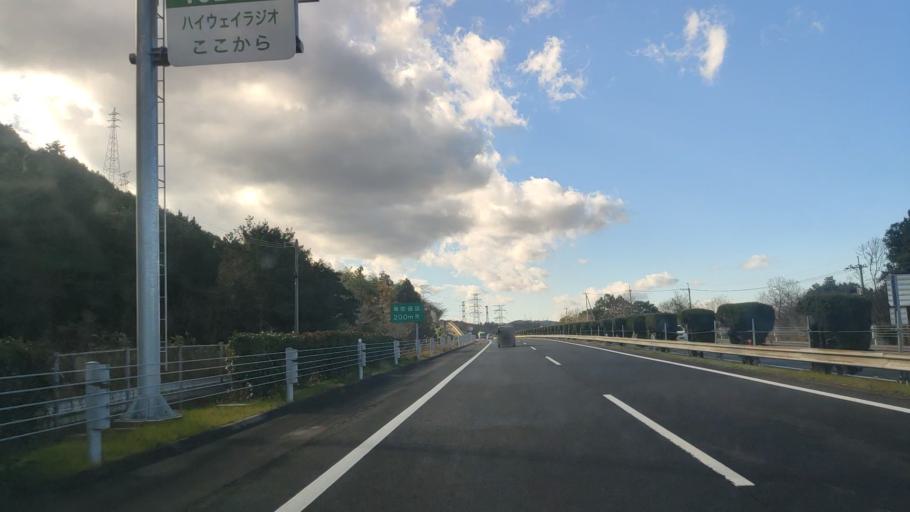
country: JP
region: Ehime
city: Niihama
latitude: 33.9453
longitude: 133.4108
